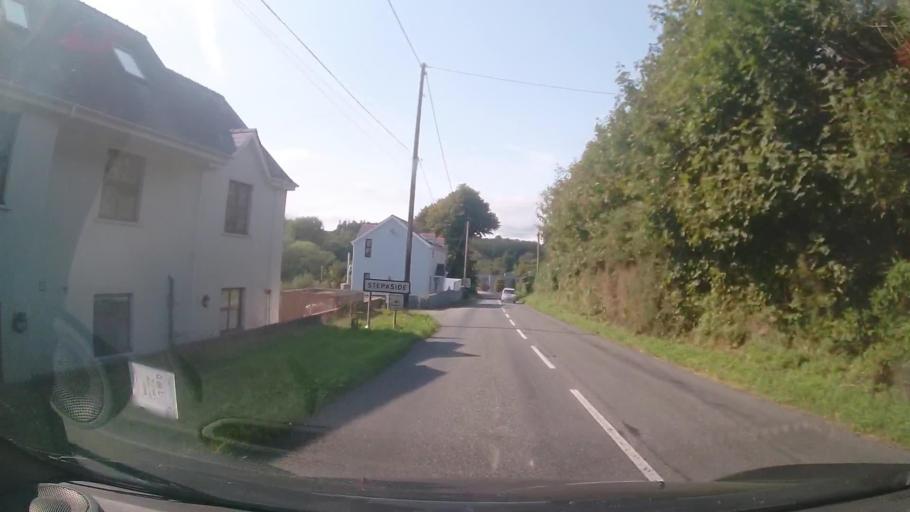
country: GB
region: Wales
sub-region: Pembrokeshire
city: Kilgetty
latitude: 51.7367
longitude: -4.6950
